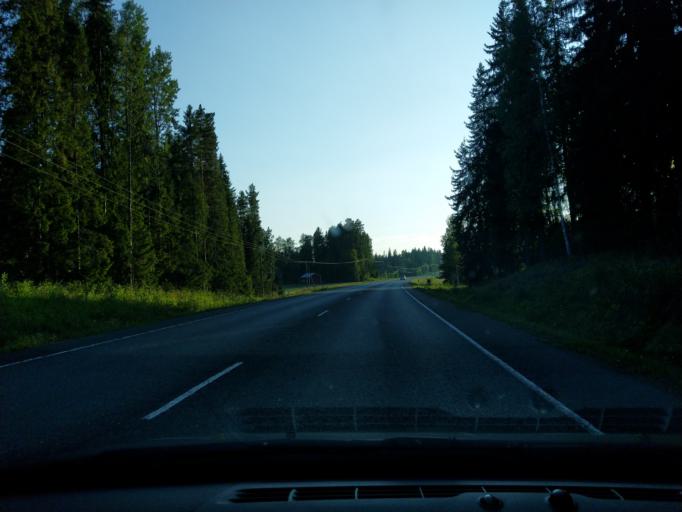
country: FI
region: Uusimaa
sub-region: Helsinki
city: Maentsaelae
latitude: 60.6252
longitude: 25.2043
